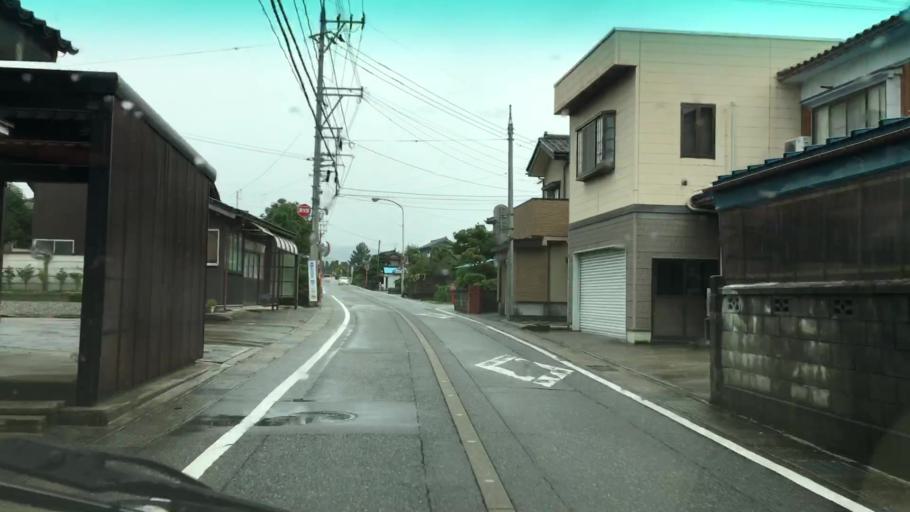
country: JP
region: Toyama
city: Kamiichi
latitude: 36.6481
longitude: 137.3199
